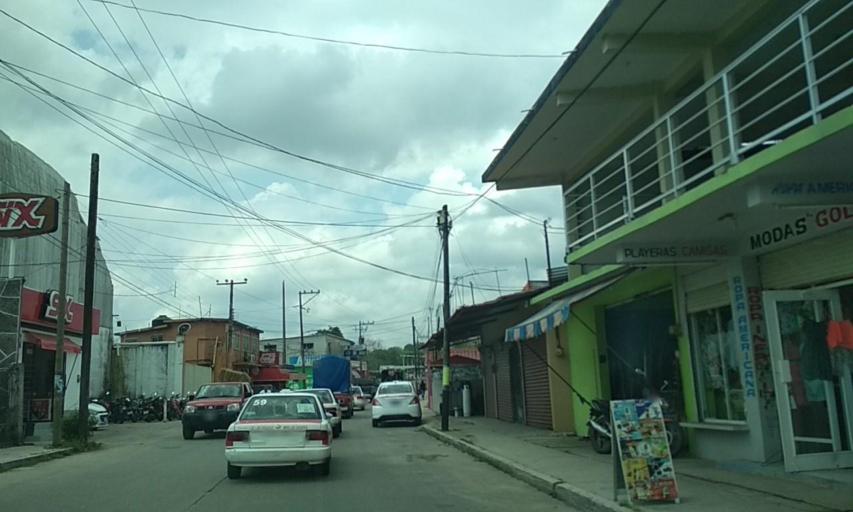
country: MX
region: Veracruz
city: Las Choapas
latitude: 17.8957
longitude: -94.1023
